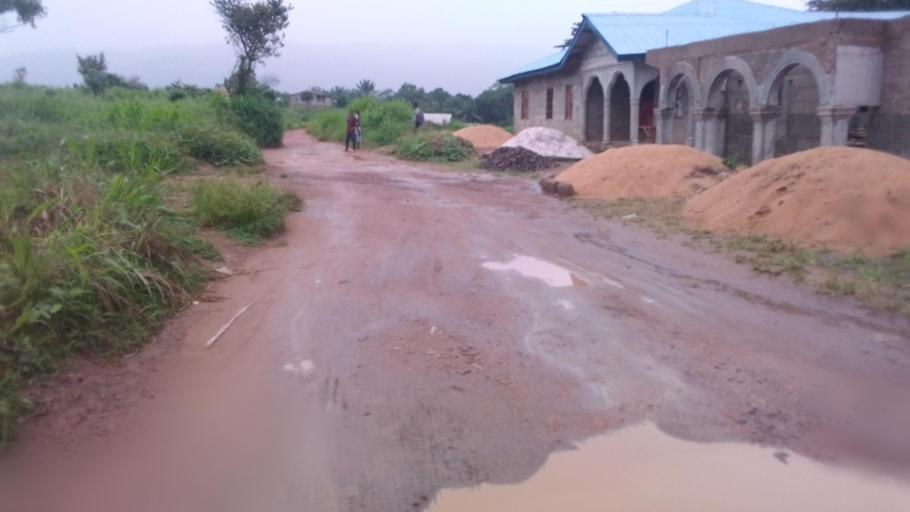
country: SL
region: Eastern Province
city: Kenema
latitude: 7.9016
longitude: -11.1636
